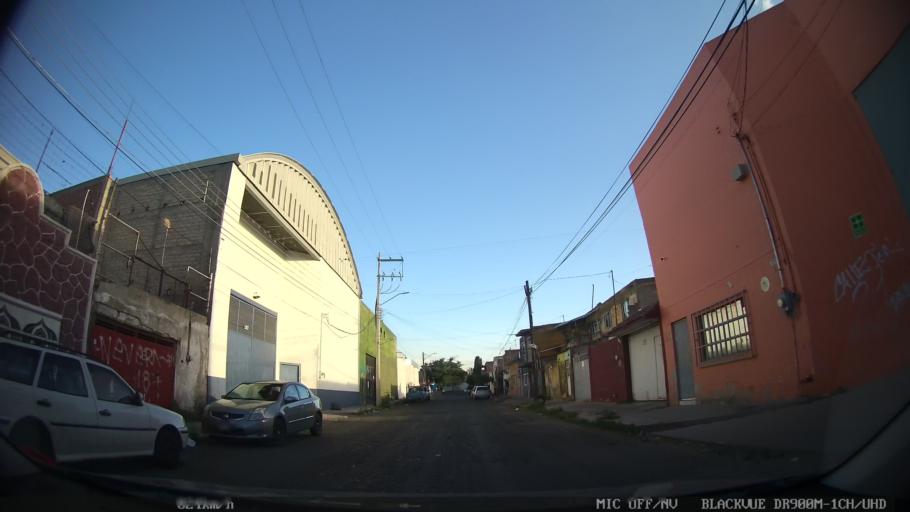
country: MX
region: Jalisco
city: Tlaquepaque
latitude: 20.7067
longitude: -103.2979
